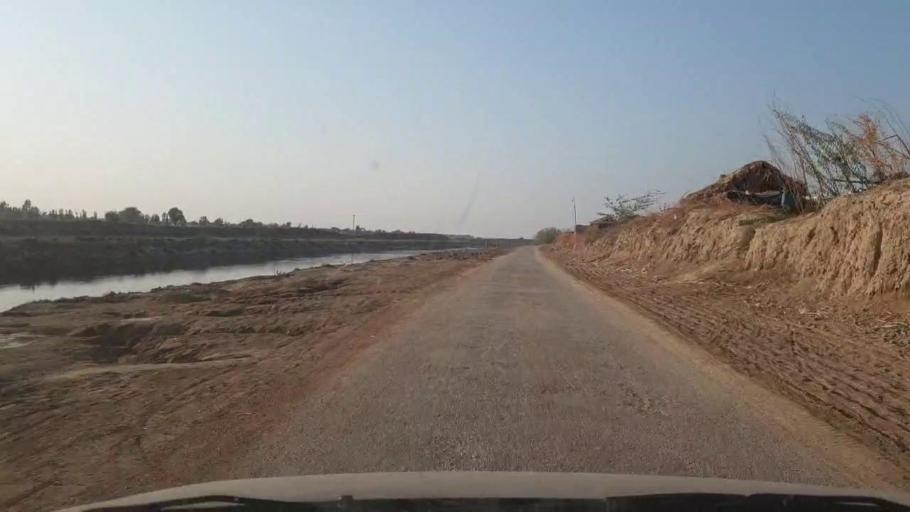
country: PK
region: Sindh
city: Samaro
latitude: 25.2871
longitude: 69.3355
